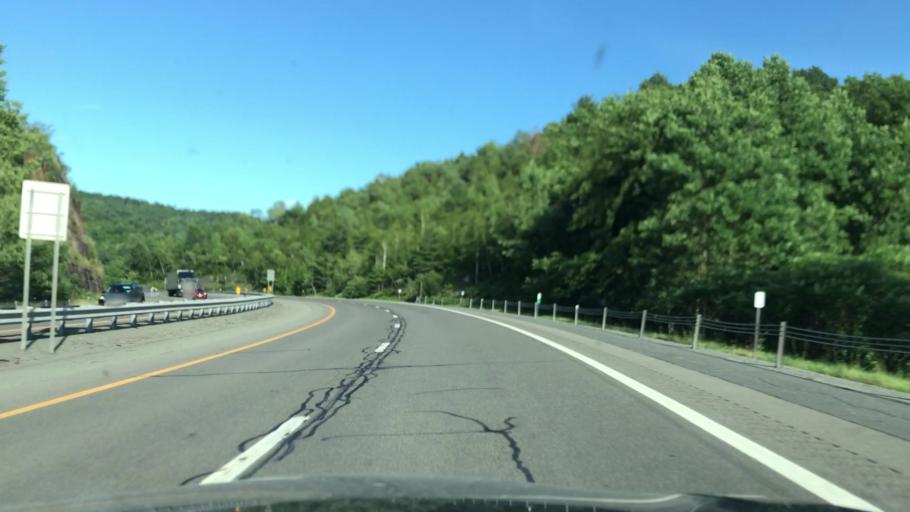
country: US
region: New York
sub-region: Delaware County
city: Hancock
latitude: 41.9562
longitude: -75.2426
